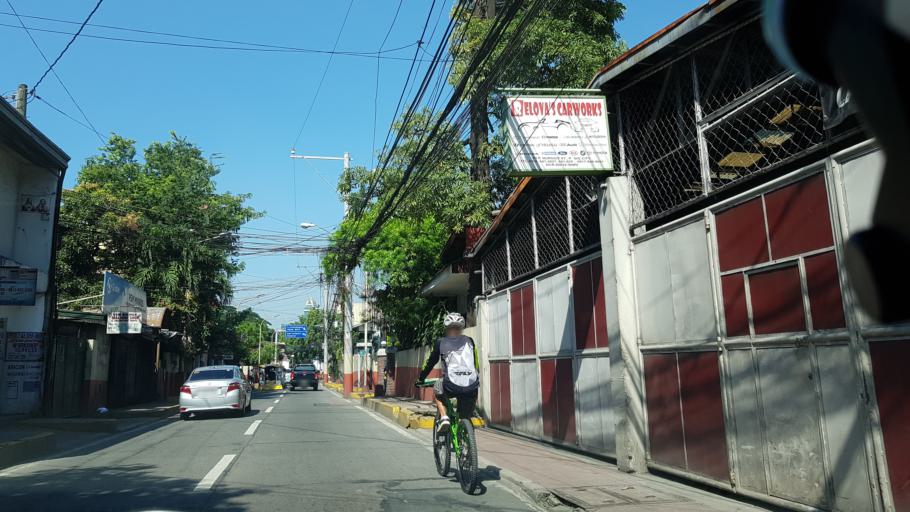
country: PH
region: Calabarzon
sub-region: Province of Rizal
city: Pateros
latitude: 14.5597
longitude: 121.0747
